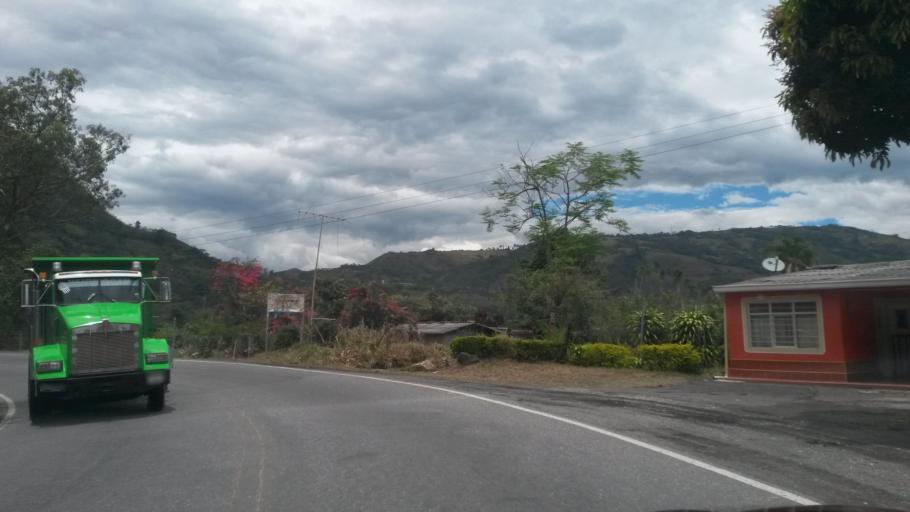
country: CO
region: Cauca
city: Rosas
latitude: 2.2538
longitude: -76.7591
